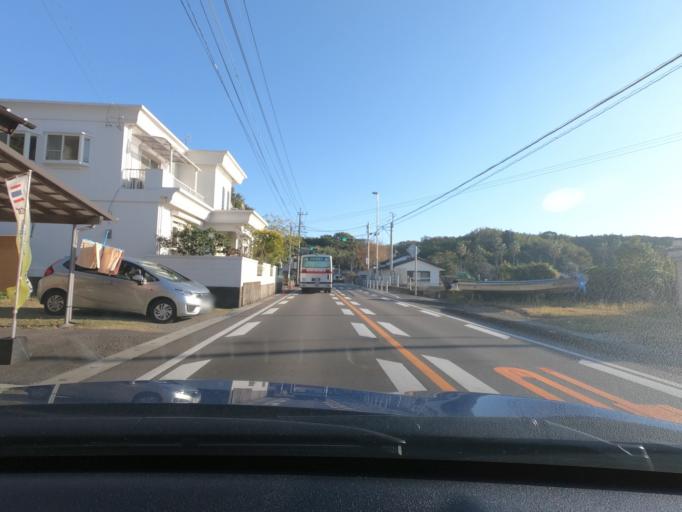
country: JP
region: Kagoshima
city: Akune
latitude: 31.9910
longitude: 130.1979
